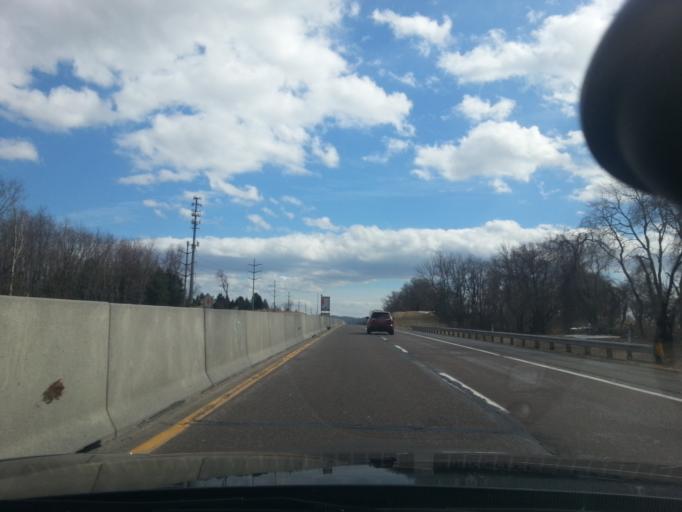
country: US
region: Pennsylvania
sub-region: Lehigh County
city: Wescosville
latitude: 40.5613
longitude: -75.5474
